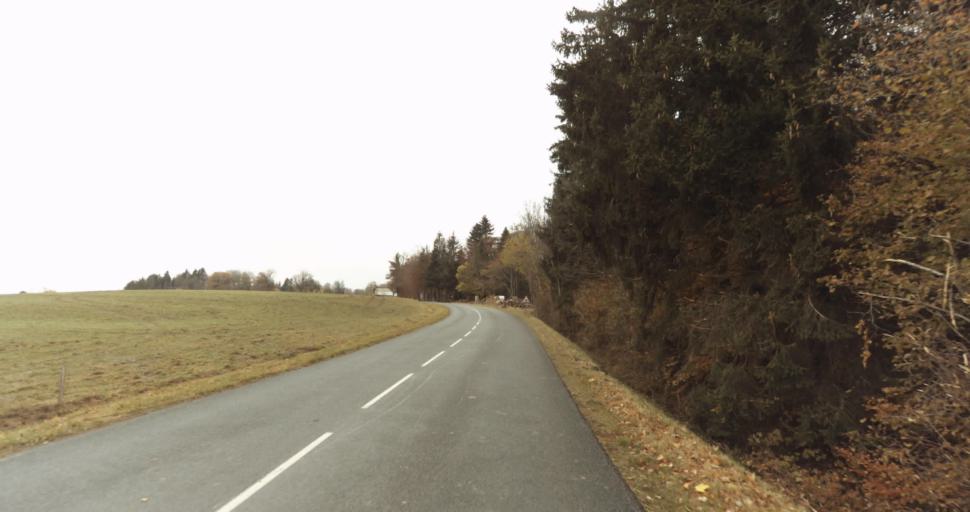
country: FR
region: Rhone-Alpes
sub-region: Departement de la Haute-Savoie
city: Evires
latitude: 46.0521
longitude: 6.2307
